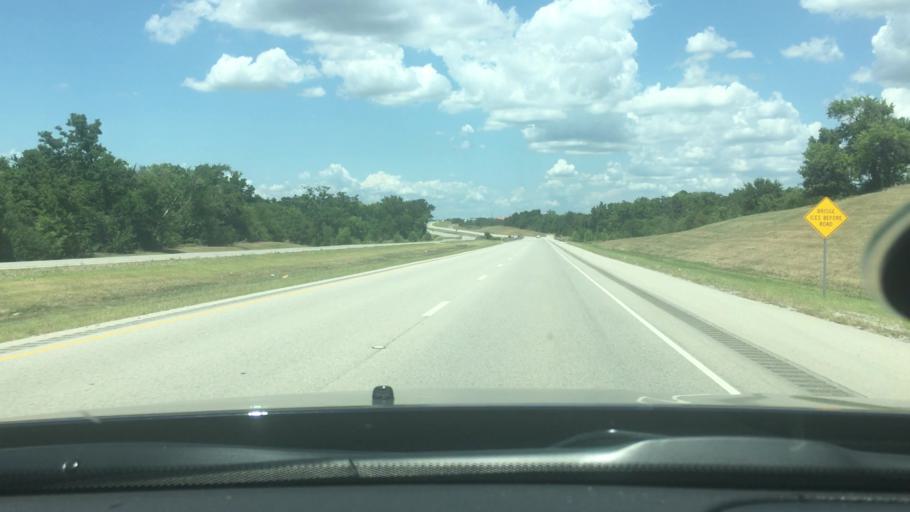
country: US
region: Oklahoma
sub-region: Bryan County
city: Calera
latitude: 33.9862
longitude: -96.4275
